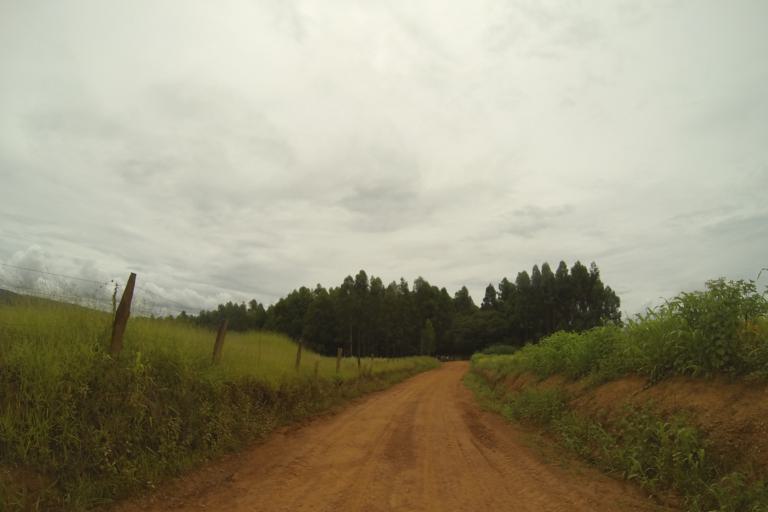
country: BR
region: Minas Gerais
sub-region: Ibia
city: Ibia
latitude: -19.7405
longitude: -46.6369
